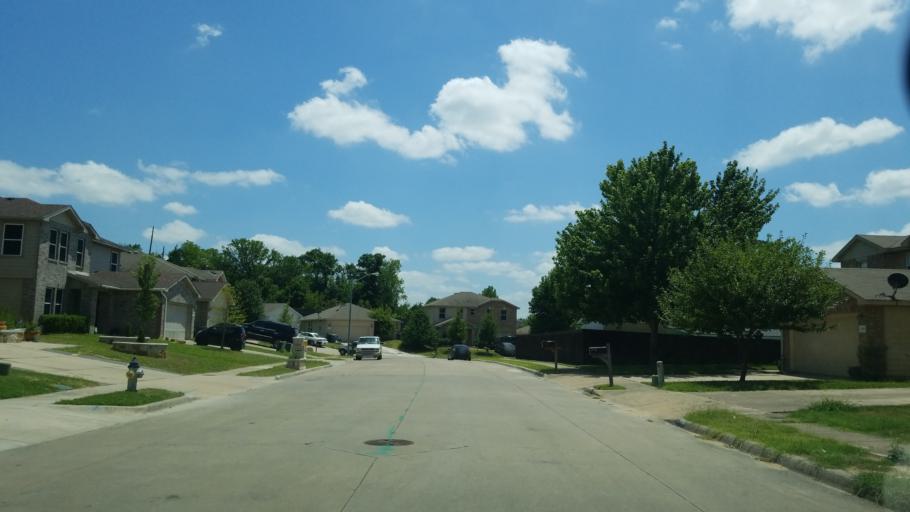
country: US
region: Texas
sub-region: Dallas County
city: Balch Springs
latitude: 32.7391
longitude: -96.7110
